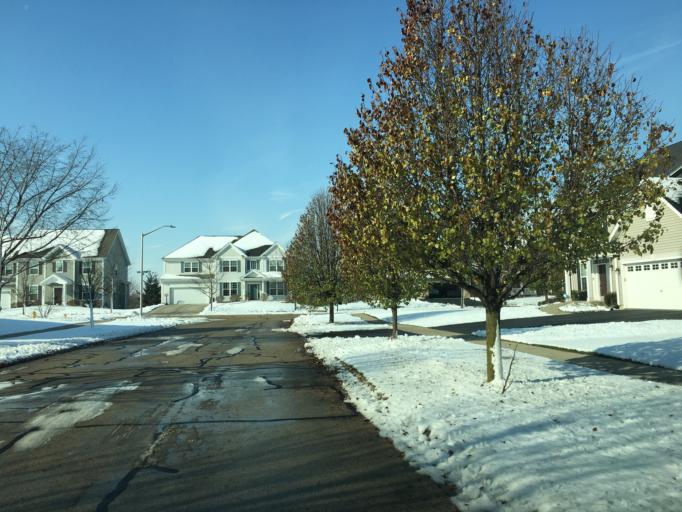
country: US
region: Illinois
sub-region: Will County
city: Plainfield
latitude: 41.6553
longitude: -88.1772
